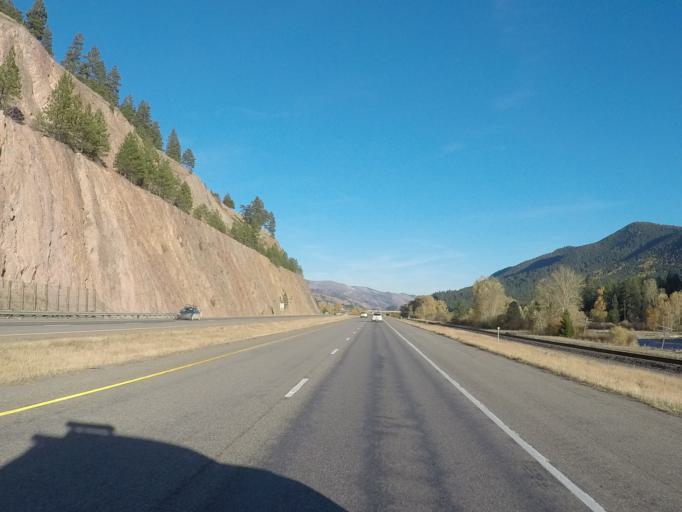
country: US
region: Montana
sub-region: Missoula County
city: Clinton
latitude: 46.7261
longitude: -113.6857
